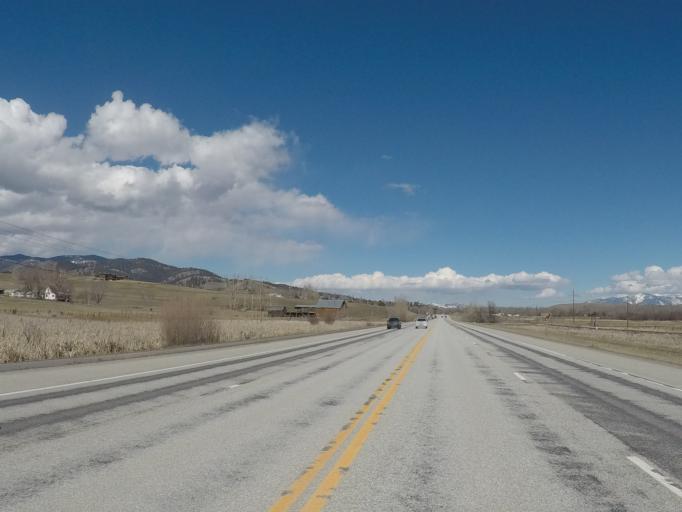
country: US
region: Montana
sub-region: Missoula County
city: Lolo
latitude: 46.7339
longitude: -114.0800
